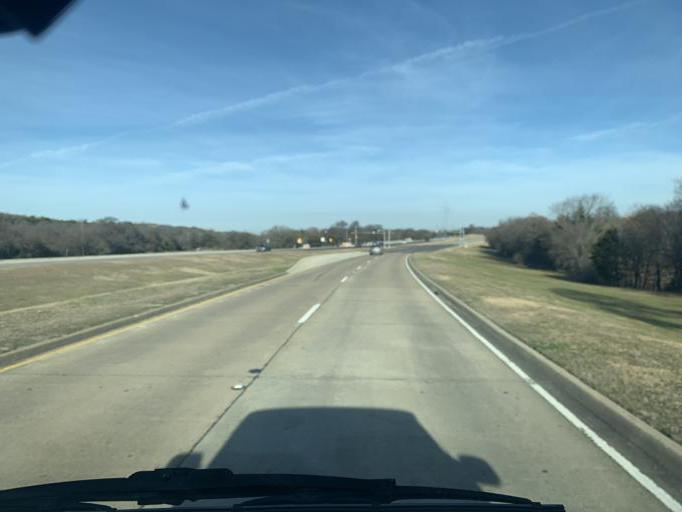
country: US
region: Texas
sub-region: Dallas County
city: Cedar Hill
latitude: 32.6178
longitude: -96.9741
